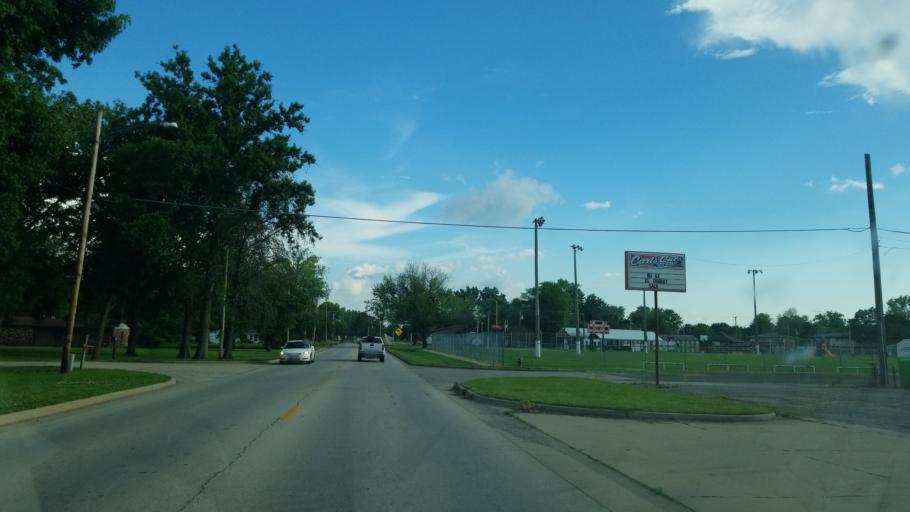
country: US
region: Illinois
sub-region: Marion County
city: Sandoval
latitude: 38.6102
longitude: -89.1152
